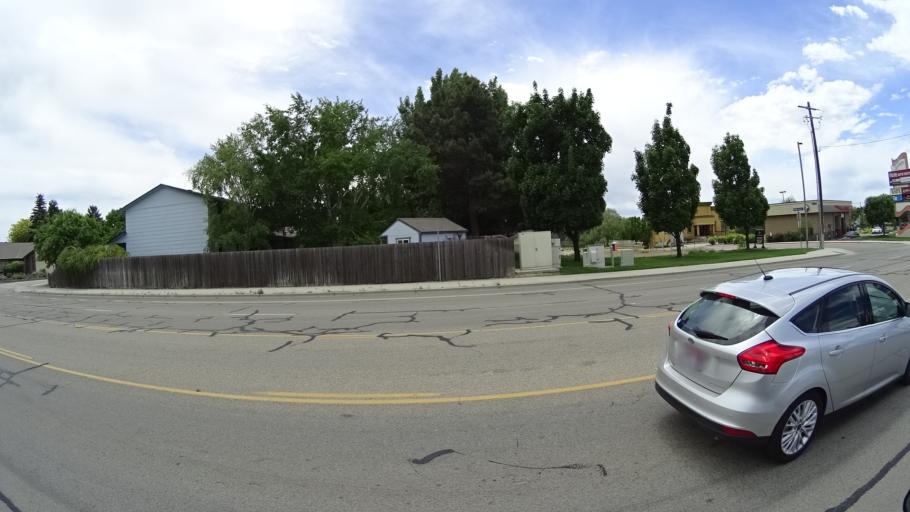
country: US
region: Idaho
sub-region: Ada County
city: Meridian
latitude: 43.5901
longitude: -116.3916
